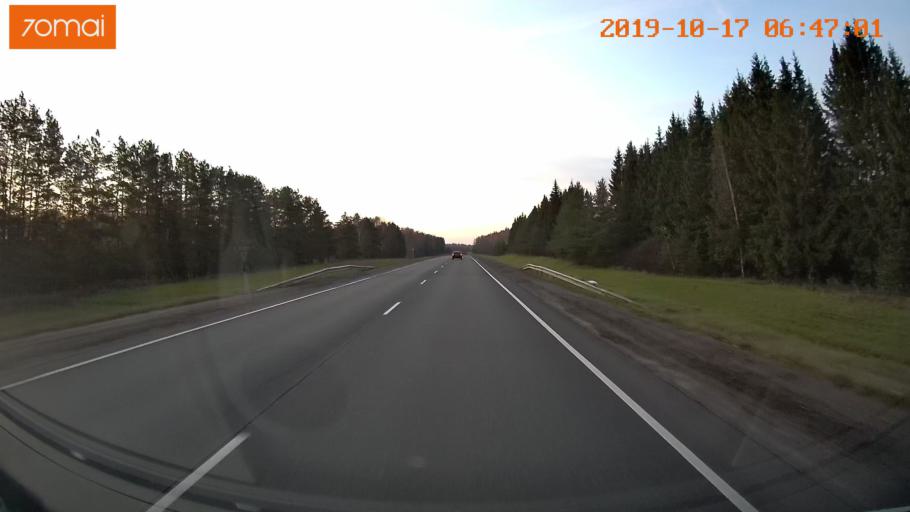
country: RU
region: Vladimir
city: Kideksha
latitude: 56.5417
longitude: 40.5549
